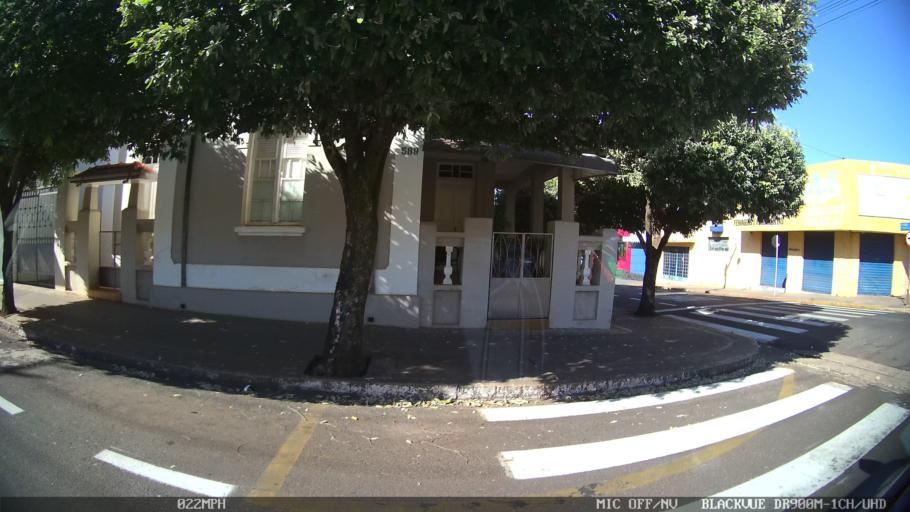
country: BR
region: Sao Paulo
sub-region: Olimpia
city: Olimpia
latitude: -20.7404
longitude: -48.9169
